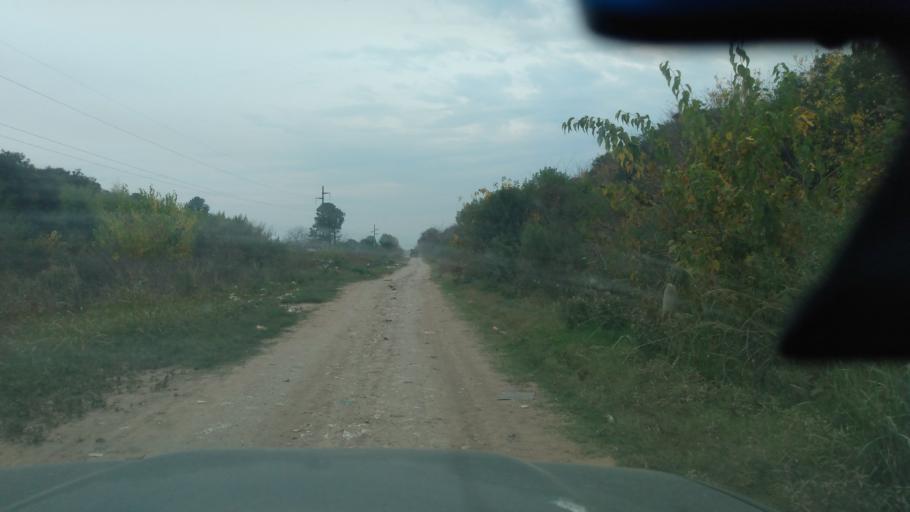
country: AR
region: Buenos Aires
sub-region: Partido de Lujan
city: Lujan
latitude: -34.5576
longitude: -59.1469
